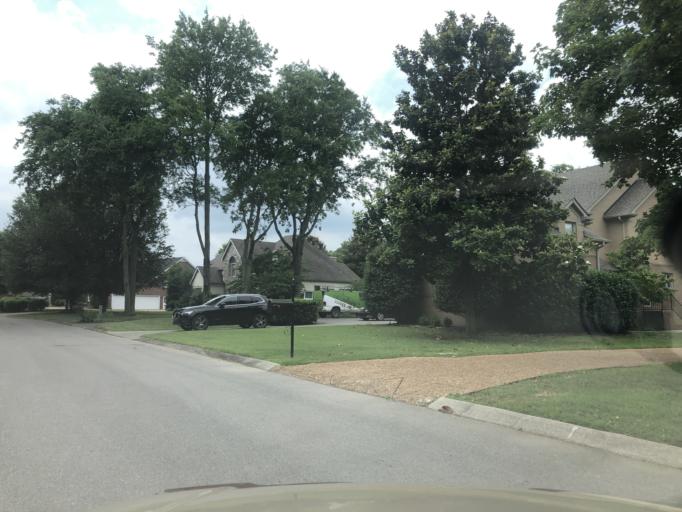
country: US
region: Tennessee
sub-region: Davidson County
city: Lakewood
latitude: 36.2339
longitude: -86.6087
